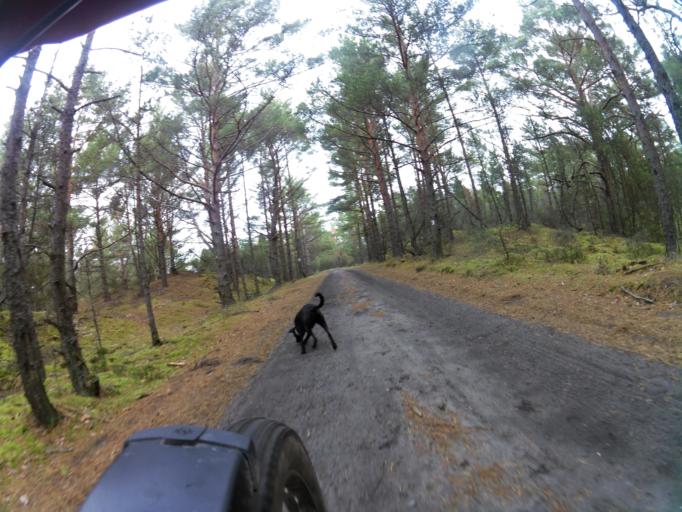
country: PL
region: Pomeranian Voivodeship
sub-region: Powiat pucki
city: Hel
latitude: 54.6187
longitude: 18.8192
